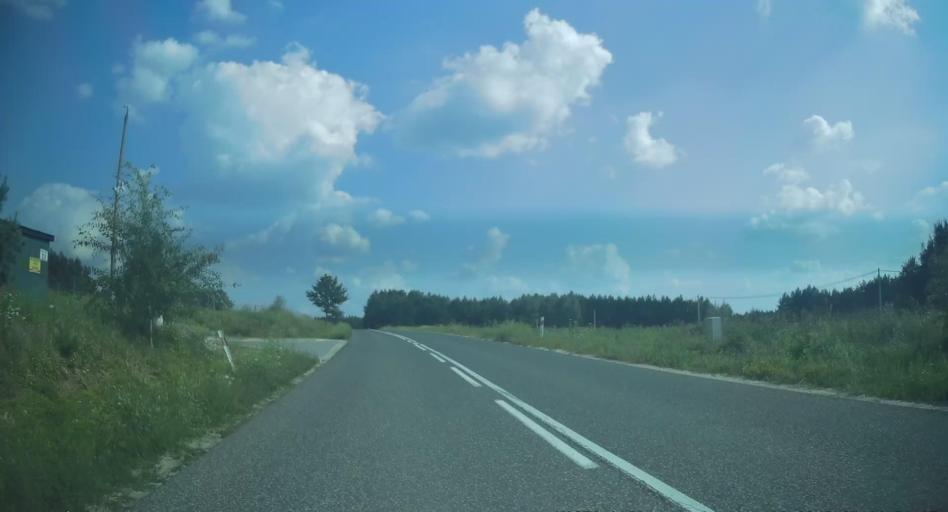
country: PL
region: Swietokrzyskie
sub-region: Powiat kielecki
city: Lopuszno
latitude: 50.8950
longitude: 20.2524
